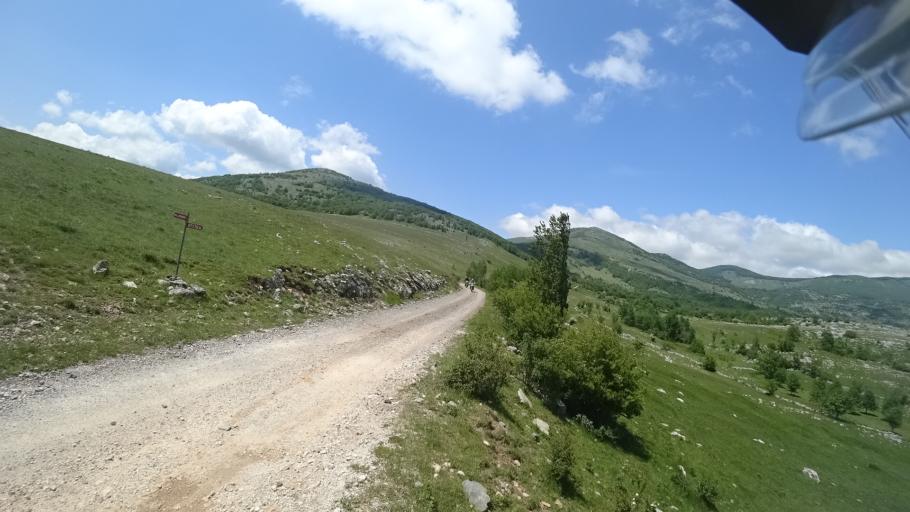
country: HR
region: Zadarska
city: Gracac
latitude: 44.4381
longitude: 15.9216
